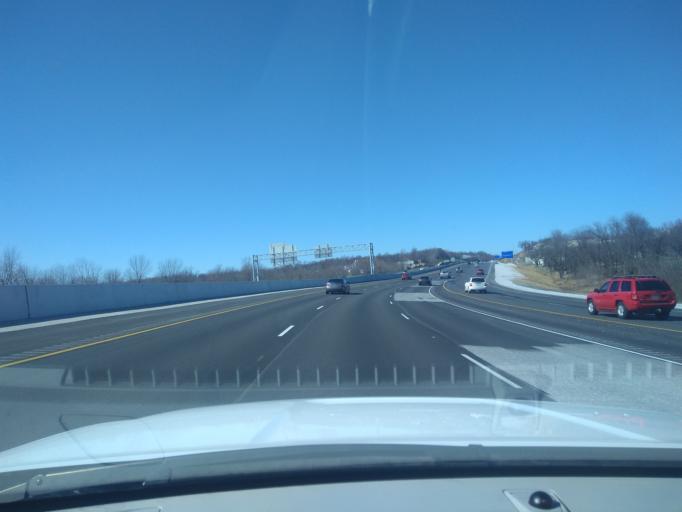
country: US
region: Arkansas
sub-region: Washington County
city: Johnson
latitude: 36.1142
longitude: -94.1749
